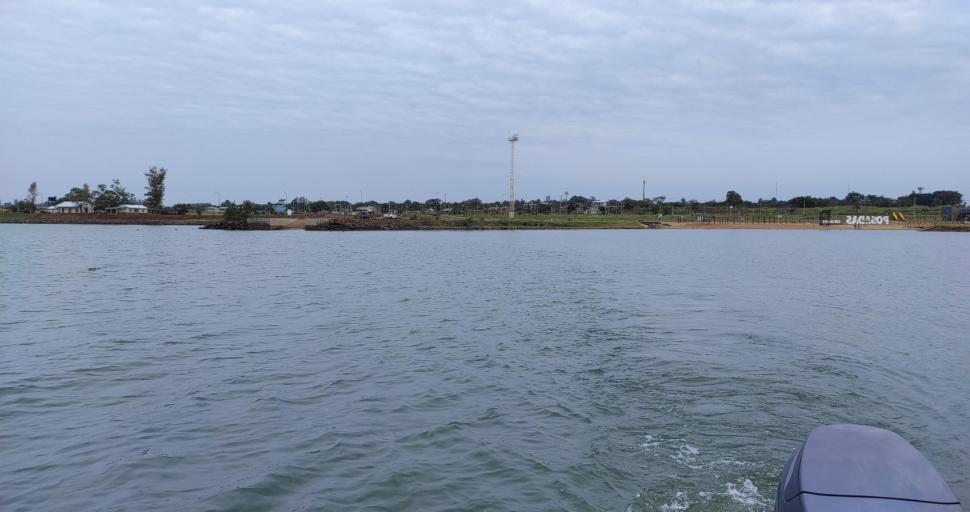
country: AR
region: Misiones
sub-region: Departamento de Capital
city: Posadas
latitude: -27.4186
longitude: -55.8746
